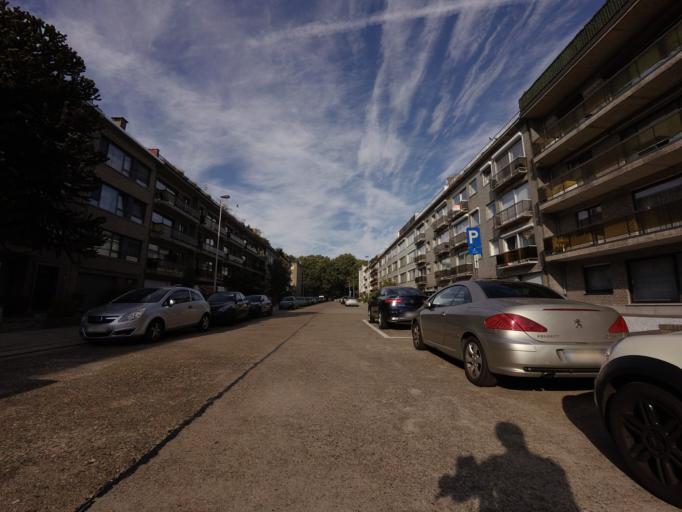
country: BE
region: Flanders
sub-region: Provincie Antwerpen
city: Schoten
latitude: 51.2307
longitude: 4.4817
